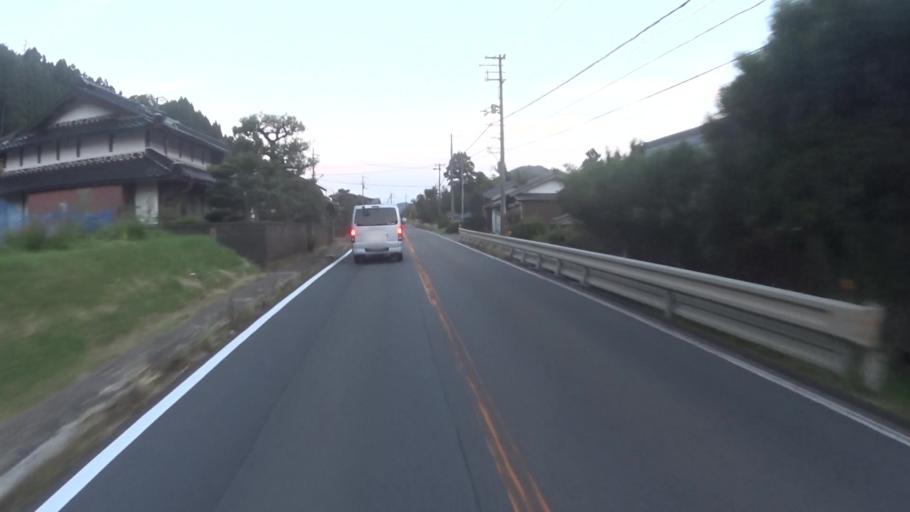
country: JP
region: Kyoto
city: Ayabe
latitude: 35.2429
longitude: 135.4169
